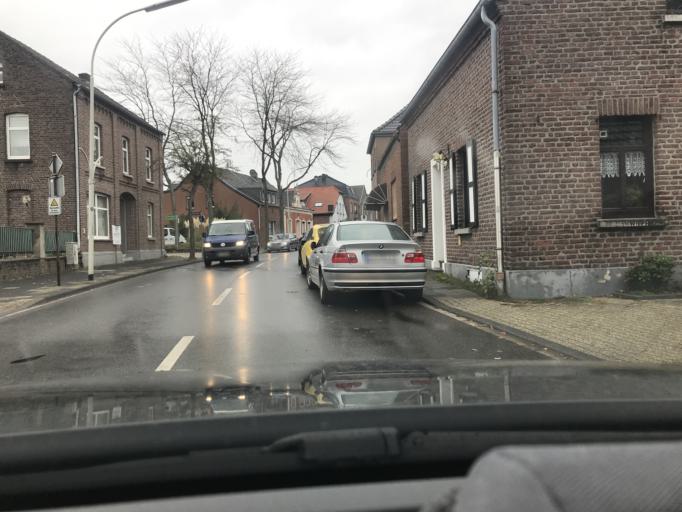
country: DE
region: North Rhine-Westphalia
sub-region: Regierungsbezirk Dusseldorf
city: Nettetal
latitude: 51.3323
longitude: 6.2800
